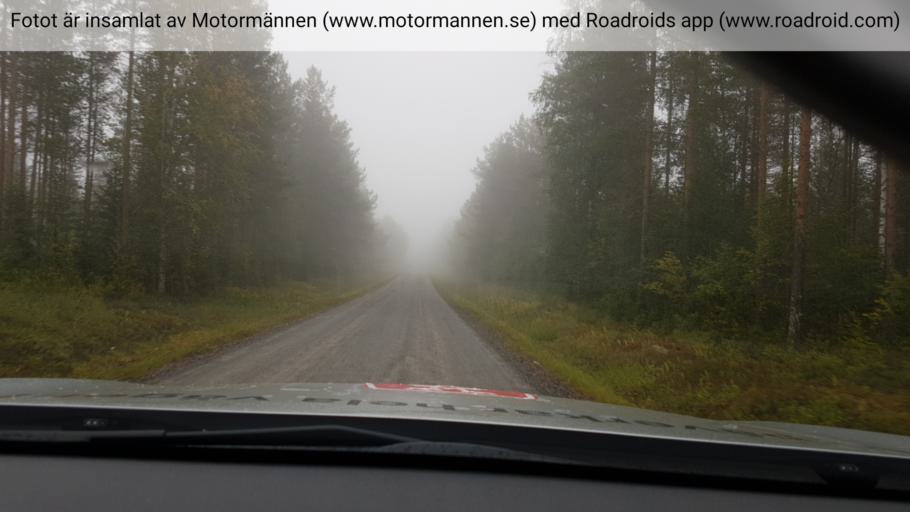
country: SE
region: Vaesterbotten
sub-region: Umea Kommun
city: Ersmark
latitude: 64.1130
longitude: 20.3506
